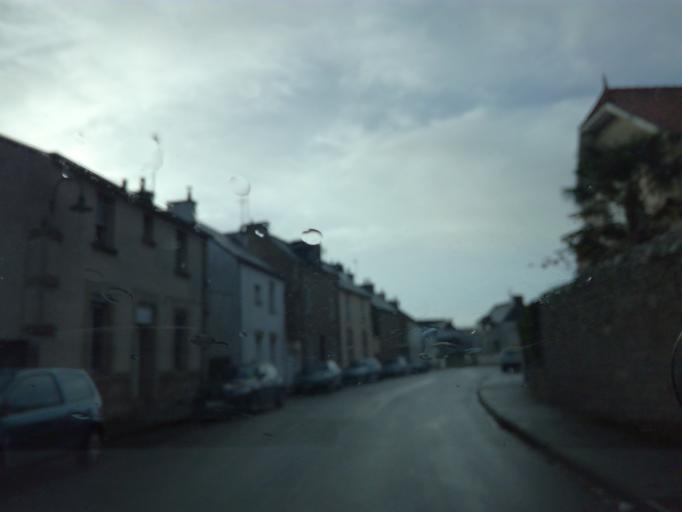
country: FR
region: Brittany
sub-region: Departement du Morbihan
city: Pontivy
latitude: 48.0580
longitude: -2.9691
